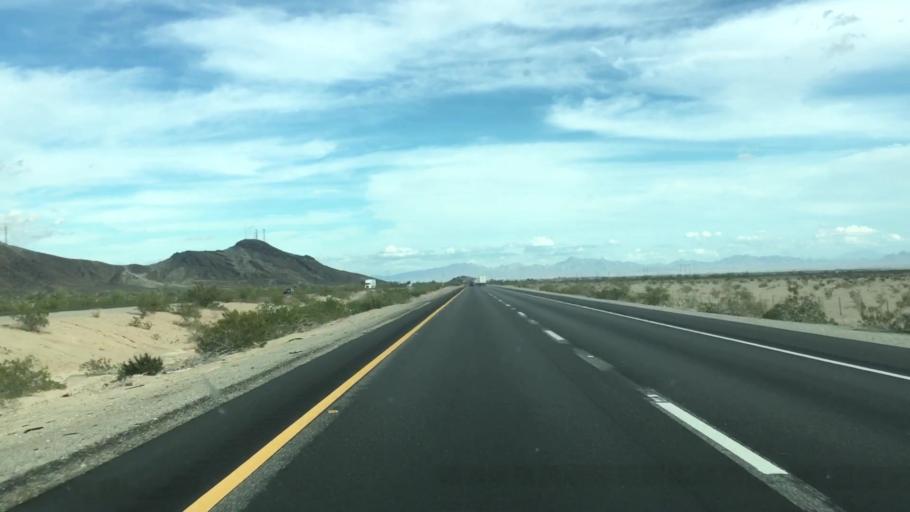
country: US
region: California
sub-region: Riverside County
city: Mesa Verde
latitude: 33.6098
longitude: -114.7900
